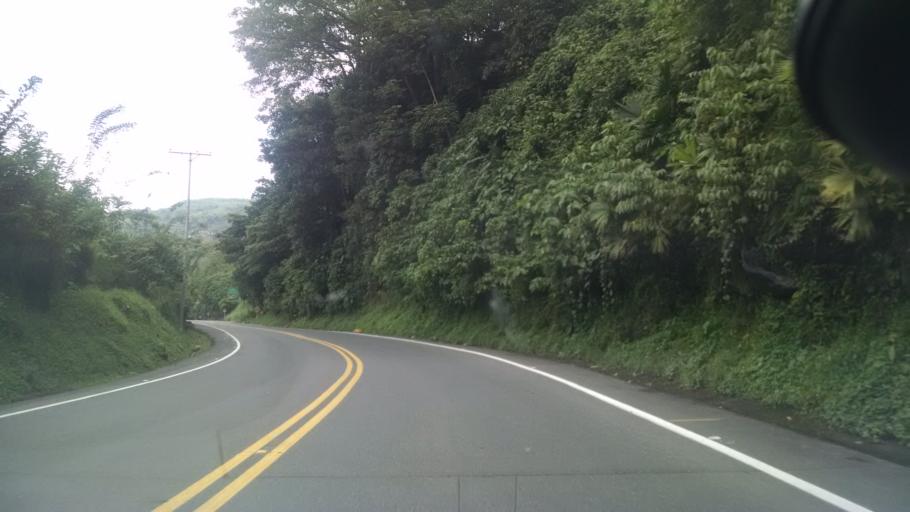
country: CO
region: Caldas
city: Palestina
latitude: 5.0551
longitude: -75.6059
